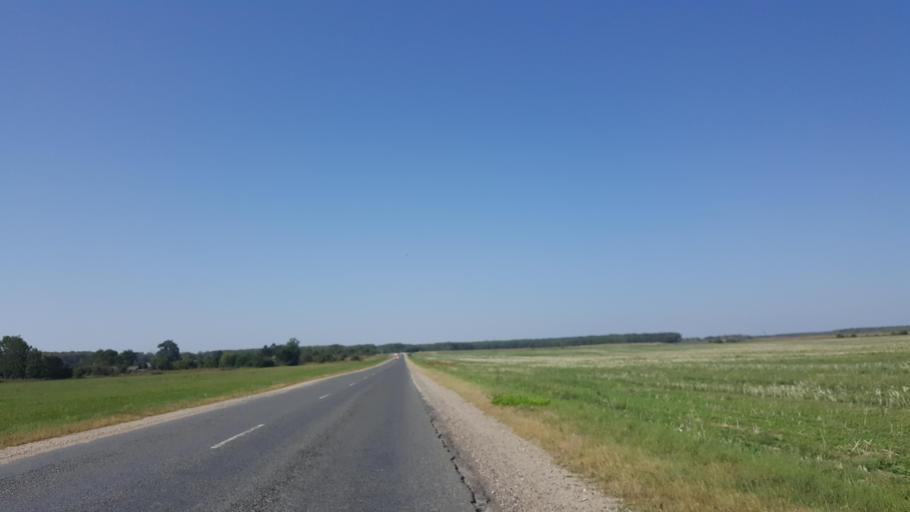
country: BY
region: Brest
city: Kamyanyets
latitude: 52.4120
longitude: 23.5970
